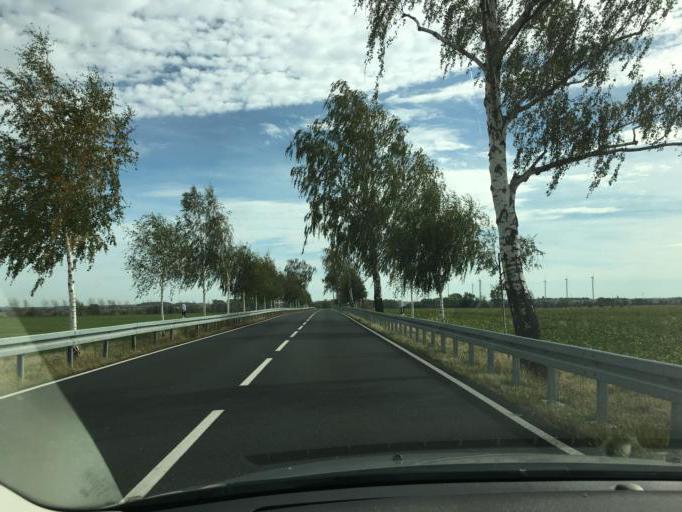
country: DE
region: Saxony
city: Lommatzsch
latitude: 51.2383
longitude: 13.3191
